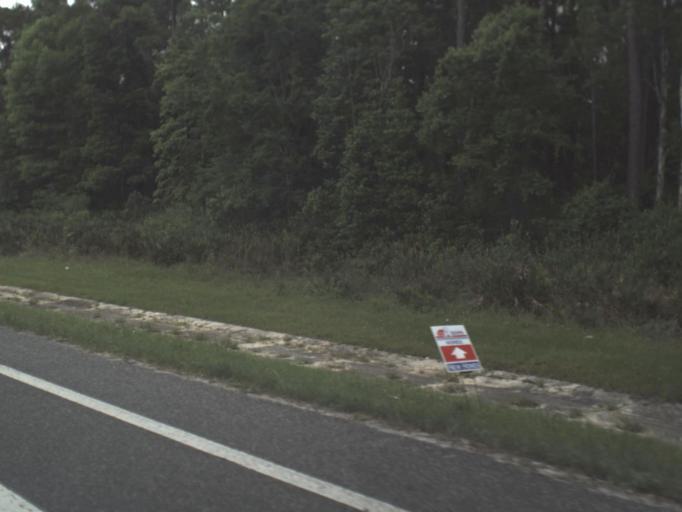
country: US
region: Florida
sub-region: Clay County
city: Middleburg
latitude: 30.0333
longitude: -81.8976
